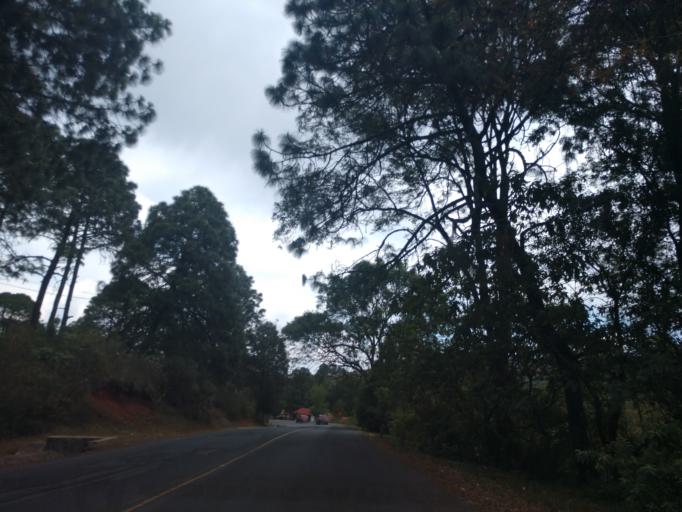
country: MX
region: Jalisco
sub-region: Mazamitla
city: Mazamitla
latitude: 19.9195
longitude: -103.0304
